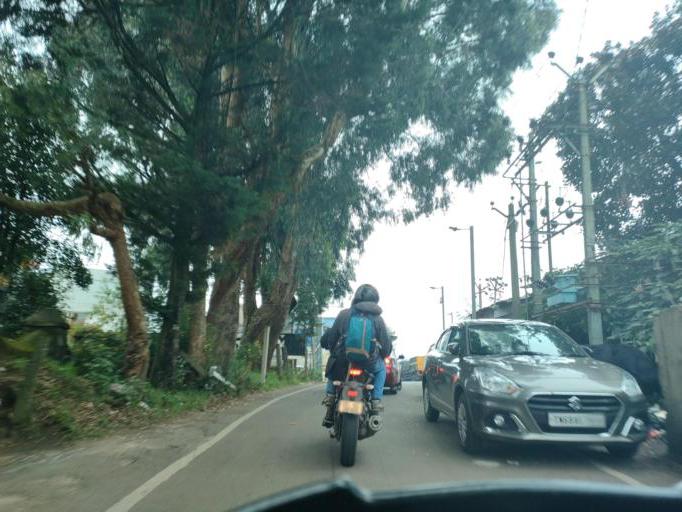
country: IN
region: Tamil Nadu
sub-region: Dindigul
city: Kodaikanal
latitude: 10.2386
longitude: 77.4854
